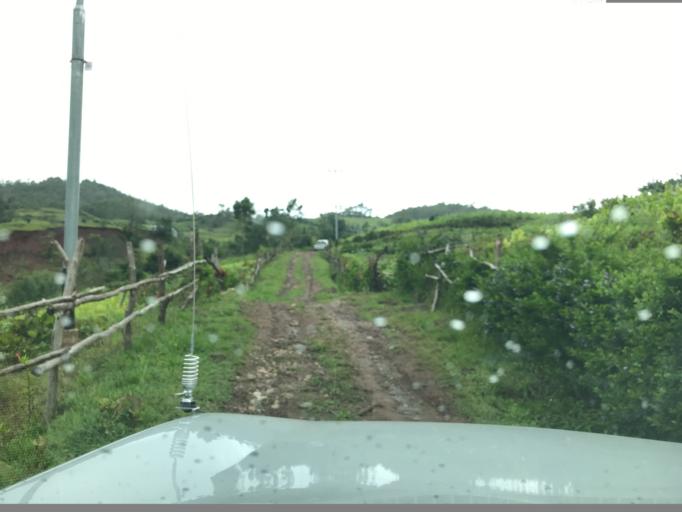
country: TL
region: Ainaro
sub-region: Ainaro
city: Ainaro
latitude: -8.8709
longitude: 125.5512
